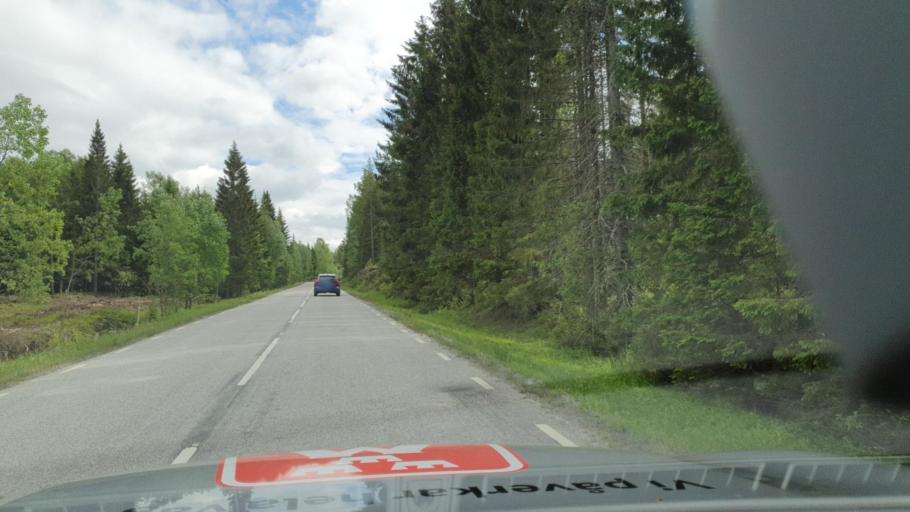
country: SE
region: Vaesternorrland
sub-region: Kramfors Kommun
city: Nordingra
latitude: 62.9160
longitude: 18.1661
